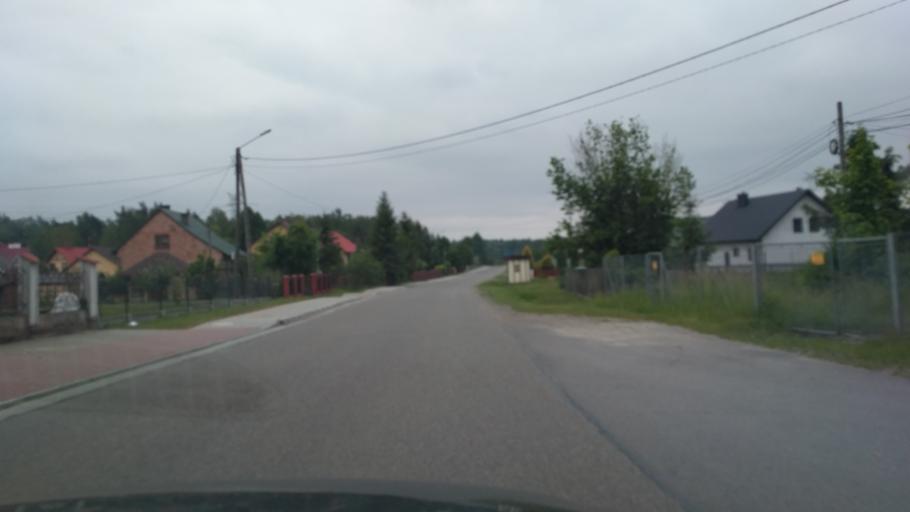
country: PL
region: Subcarpathian Voivodeship
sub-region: Powiat ropczycko-sedziszowski
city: Sedziszow Malopolski
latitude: 50.1424
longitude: 21.6700
